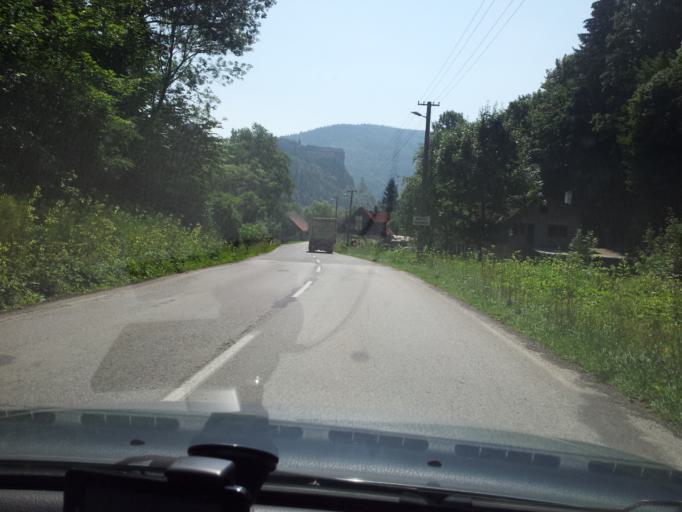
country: SK
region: Zilinsky
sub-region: Okres Dolny Kubin
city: Dolny Kubin
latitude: 49.2678
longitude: 19.3533
